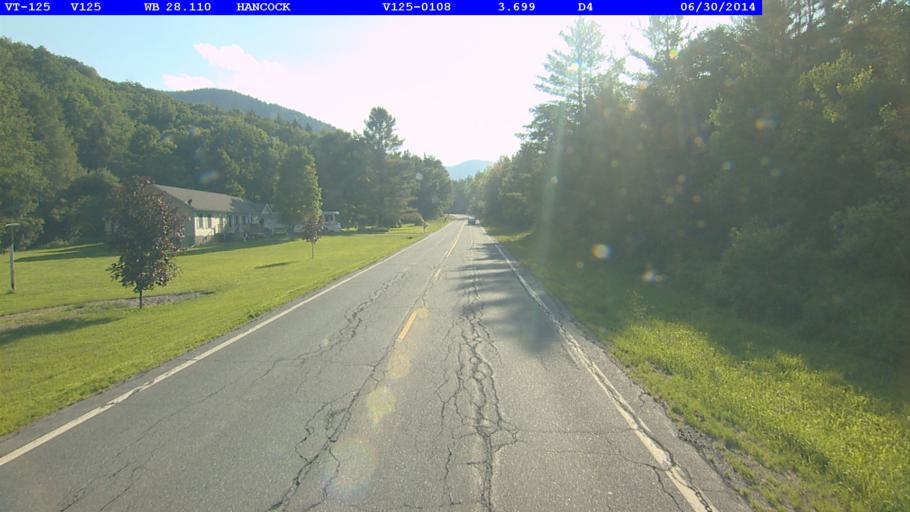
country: US
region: Vermont
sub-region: Rutland County
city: Brandon
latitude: 43.9274
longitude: -72.9089
